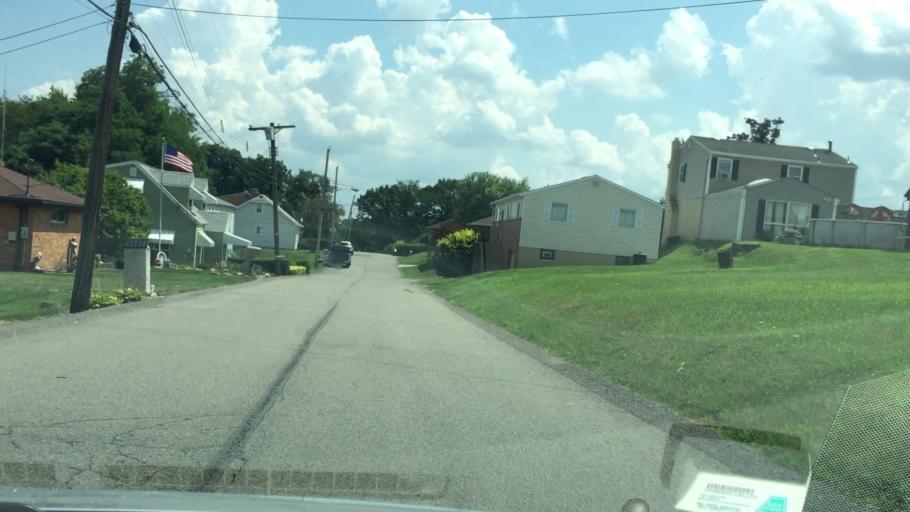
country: US
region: Pennsylvania
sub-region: Allegheny County
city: Ben Avon
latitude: 40.4870
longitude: -80.0849
